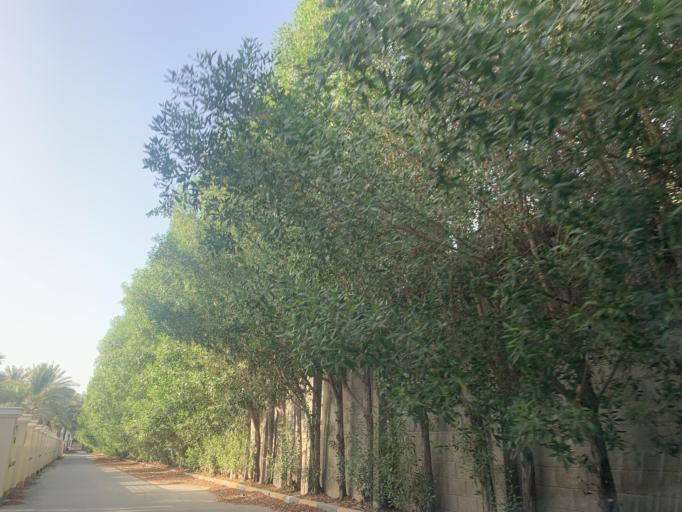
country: BH
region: Northern
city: Madinat `Isa
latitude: 26.1886
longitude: 50.4644
